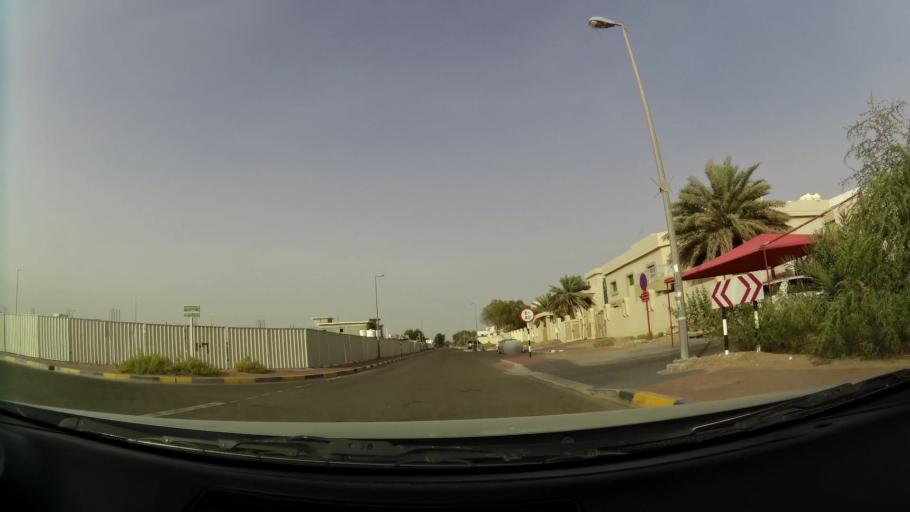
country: AE
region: Abu Dhabi
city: Al Ain
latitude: 24.2259
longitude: 55.6626
